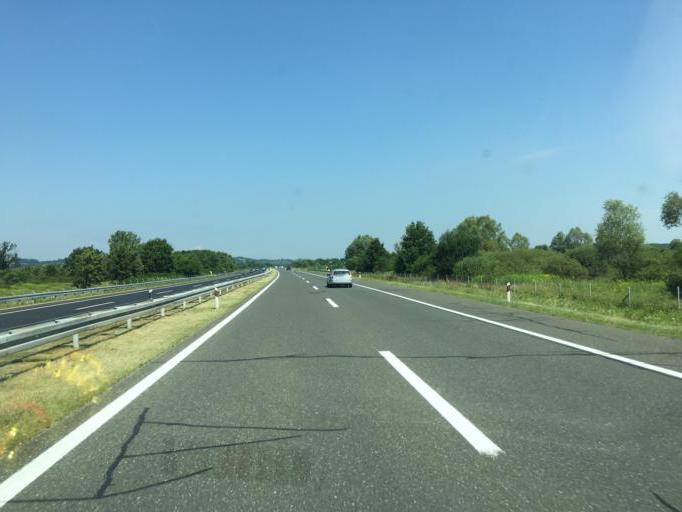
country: HR
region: Zagrebacka
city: Jablanovec
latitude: 45.8879
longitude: 15.8263
